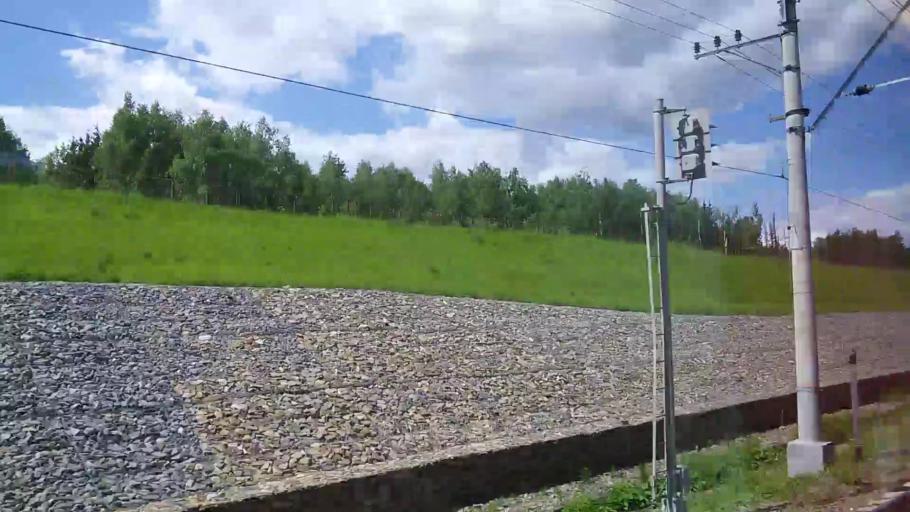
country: RU
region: Moskovskaya
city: Sheremet'yevskiy
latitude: 55.9830
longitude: 37.4683
